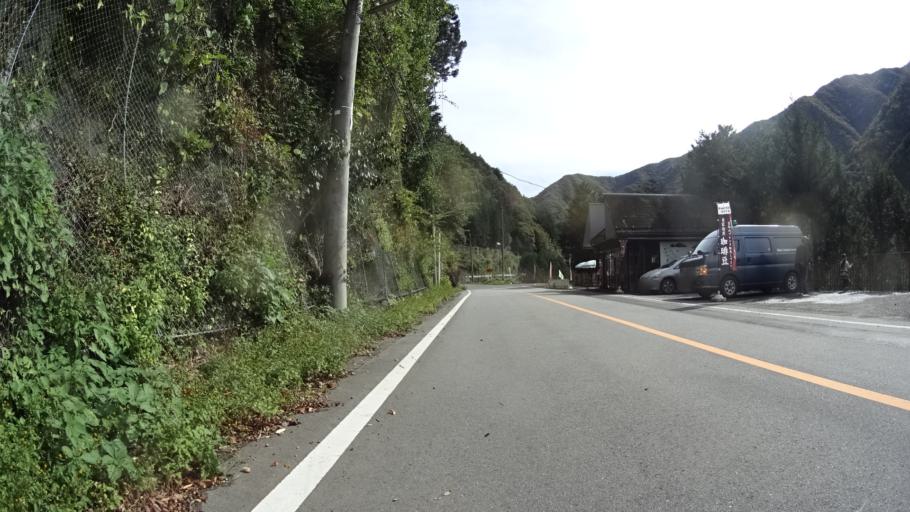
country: JP
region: Yamanashi
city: Otsuki
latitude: 35.7888
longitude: 138.9429
